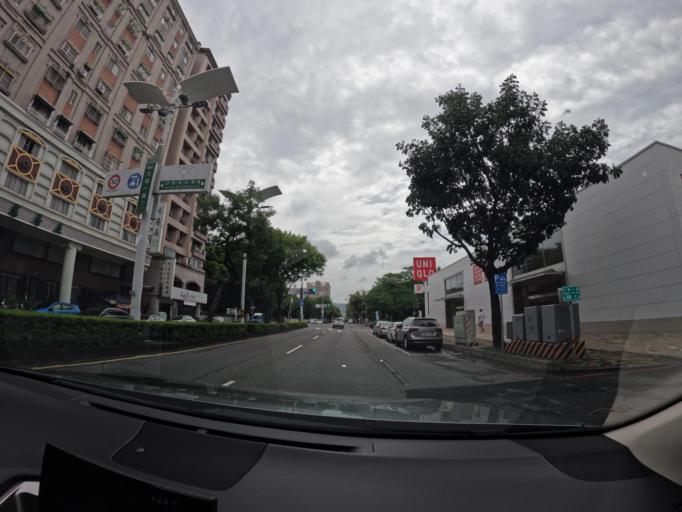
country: TW
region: Kaohsiung
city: Kaohsiung
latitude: 22.6395
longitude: 120.3253
